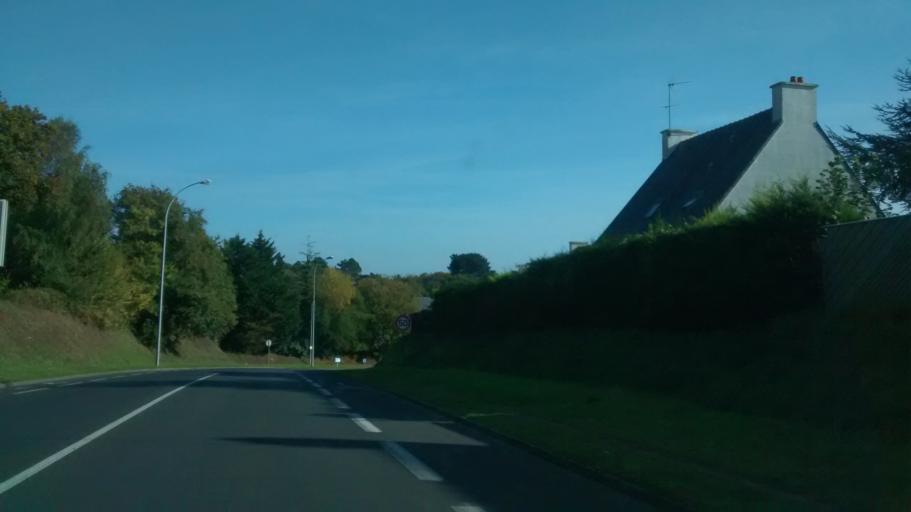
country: FR
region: Brittany
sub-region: Departement des Cotes-d'Armor
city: Lannion
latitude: 48.7470
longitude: -3.4578
